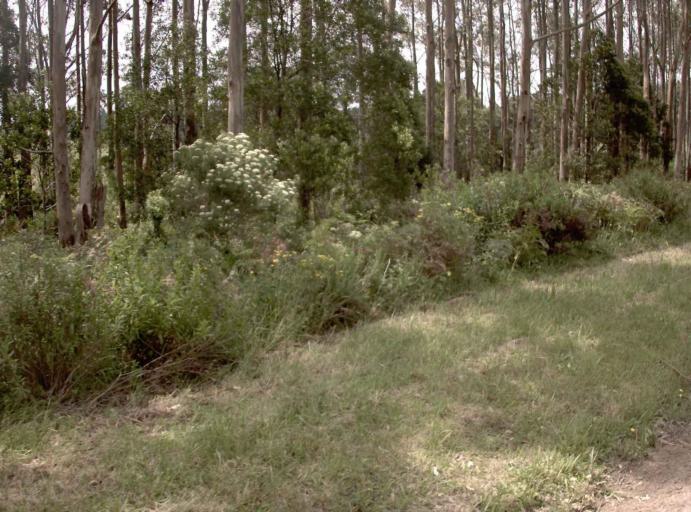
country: AU
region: Victoria
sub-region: Latrobe
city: Traralgon
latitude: -38.4048
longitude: 146.6410
